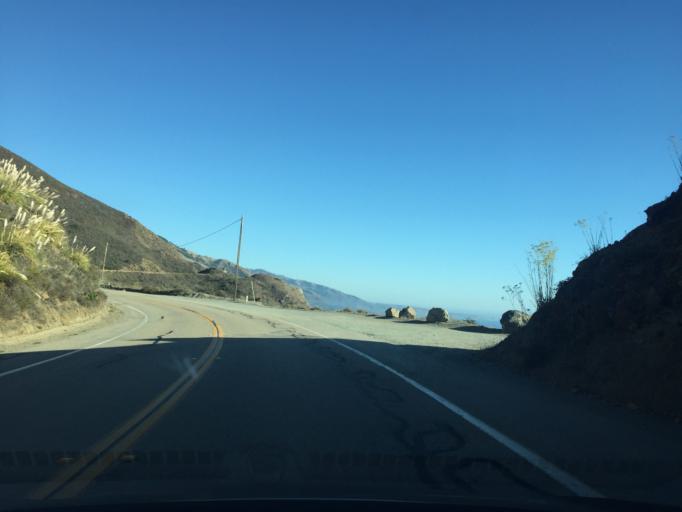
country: US
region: California
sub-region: San Luis Obispo County
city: Cambria
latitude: 35.8262
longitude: -121.3858
